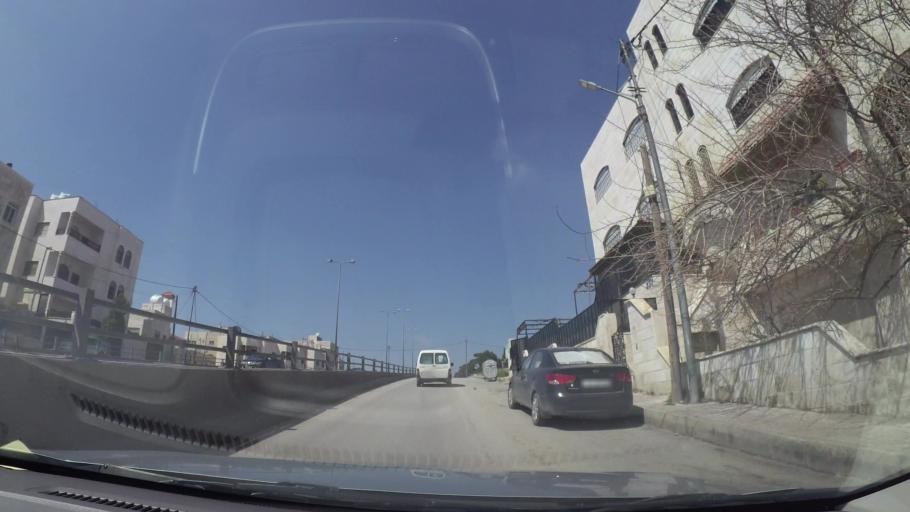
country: JO
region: Amman
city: Al Bunayyat ash Shamaliyah
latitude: 31.9193
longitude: 35.8965
